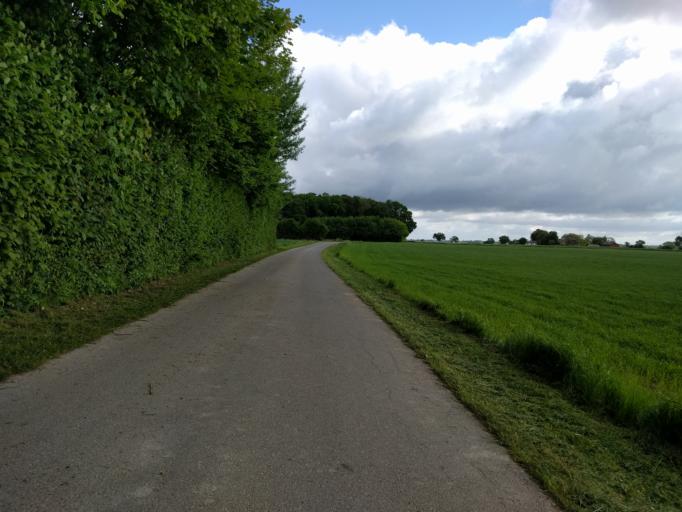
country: DK
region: South Denmark
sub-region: Kerteminde Kommune
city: Kerteminde
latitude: 55.4186
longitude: 10.6262
